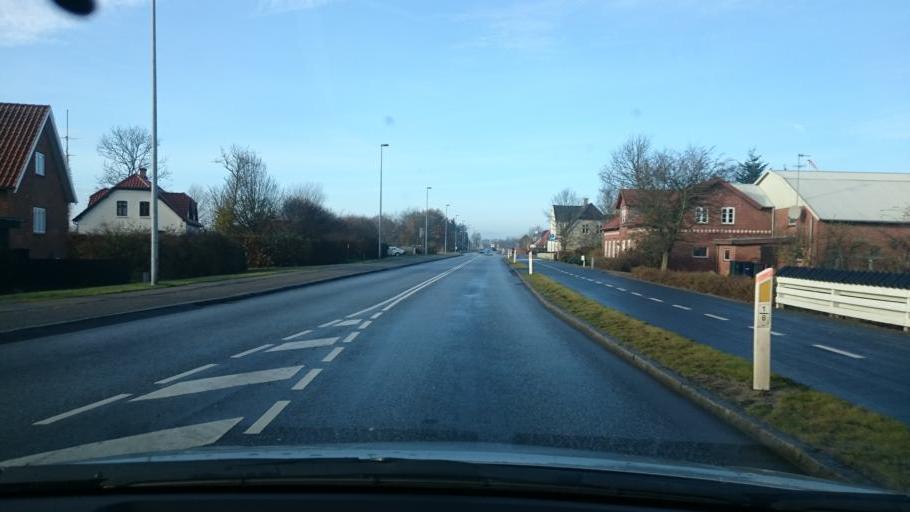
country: DK
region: South Denmark
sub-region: Esbjerg Kommune
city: Ribe
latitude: 55.3176
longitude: 8.7745
